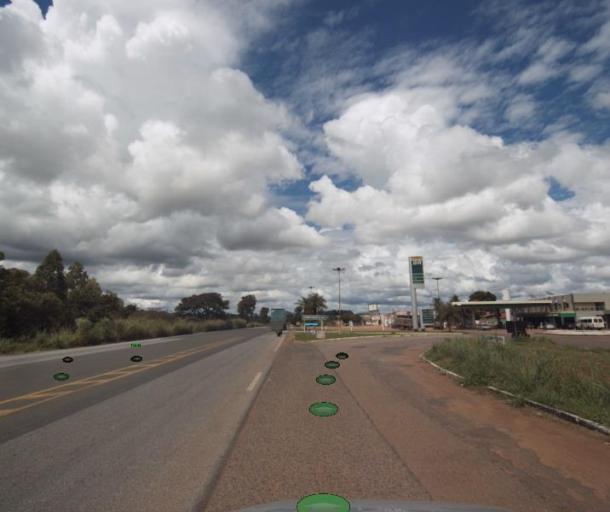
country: BR
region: Goias
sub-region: Uruacu
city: Uruacu
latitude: -14.3148
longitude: -49.1503
